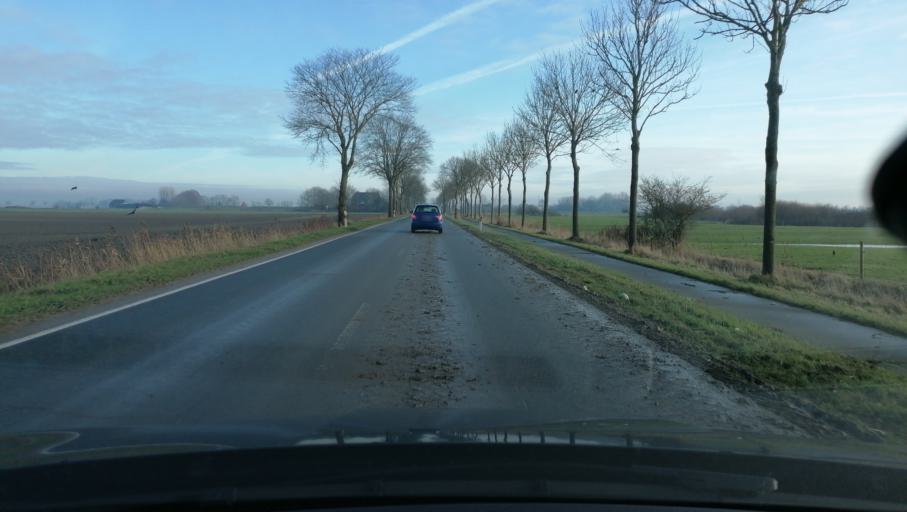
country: DE
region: Schleswig-Holstein
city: Wohrden
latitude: 54.1213
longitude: 9.0019
